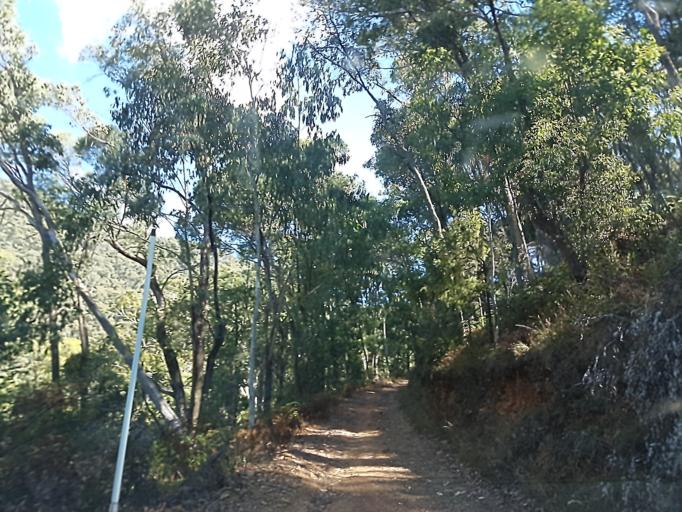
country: AU
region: Victoria
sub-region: Alpine
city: Mount Beauty
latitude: -36.8809
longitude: 147.0403
